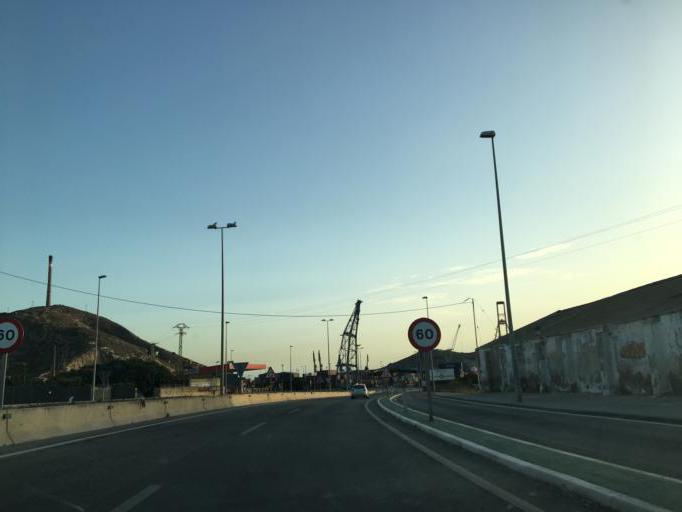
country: ES
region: Murcia
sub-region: Murcia
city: Cartagena
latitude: 37.5964
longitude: -0.9674
